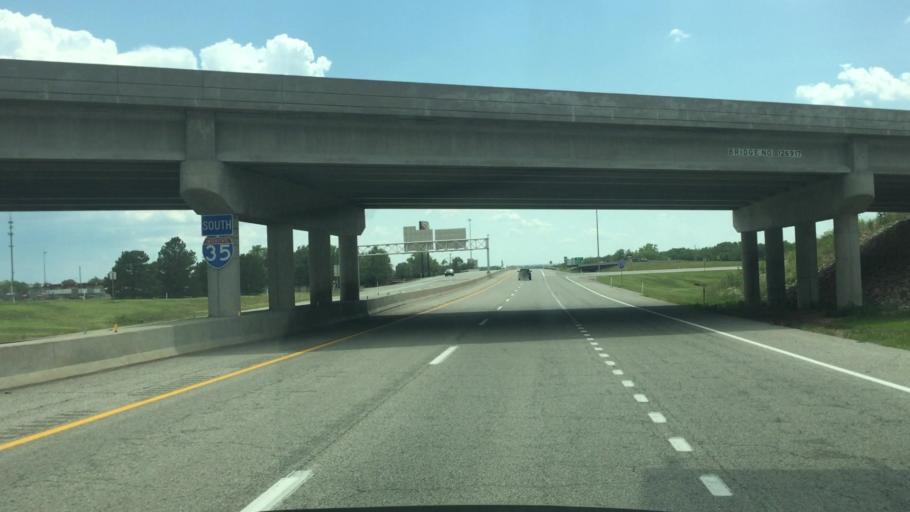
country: US
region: Kansas
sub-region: Lyon County
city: Emporia
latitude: 38.4151
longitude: -96.2375
